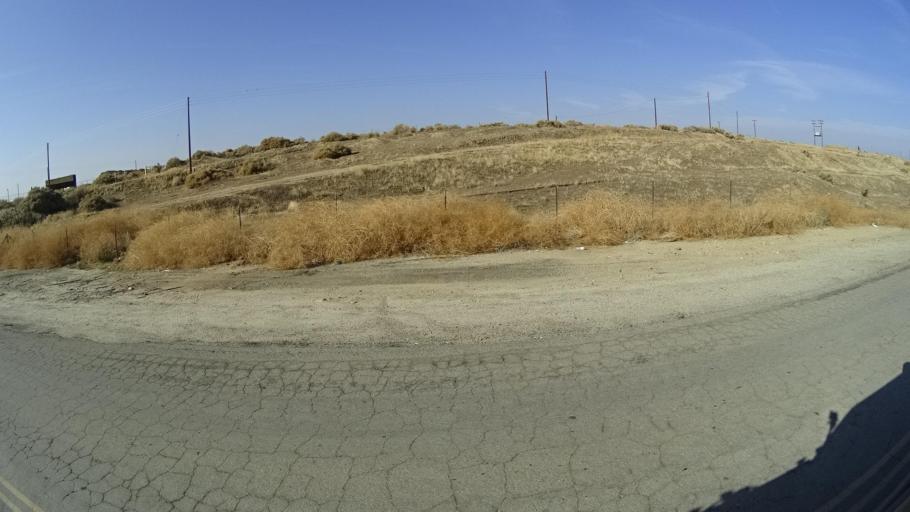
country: US
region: California
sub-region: Kern County
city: Oildale
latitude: 35.4624
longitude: -119.0489
